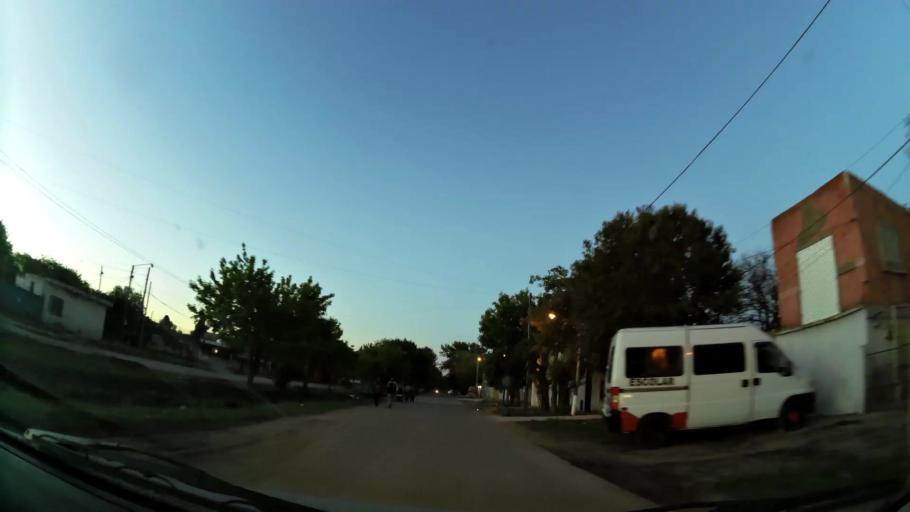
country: AR
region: Buenos Aires
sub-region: Partido de Almirante Brown
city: Adrogue
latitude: -34.7826
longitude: -58.3239
